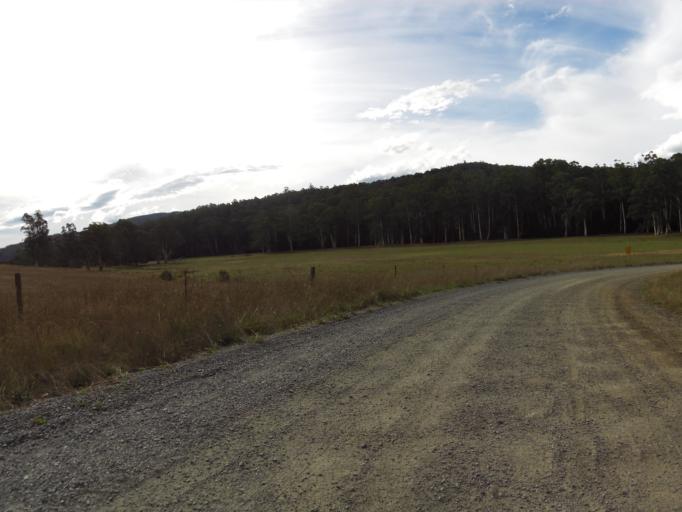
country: AU
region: Victoria
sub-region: Baw Baw
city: Warragul
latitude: -37.8965
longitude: 145.9591
